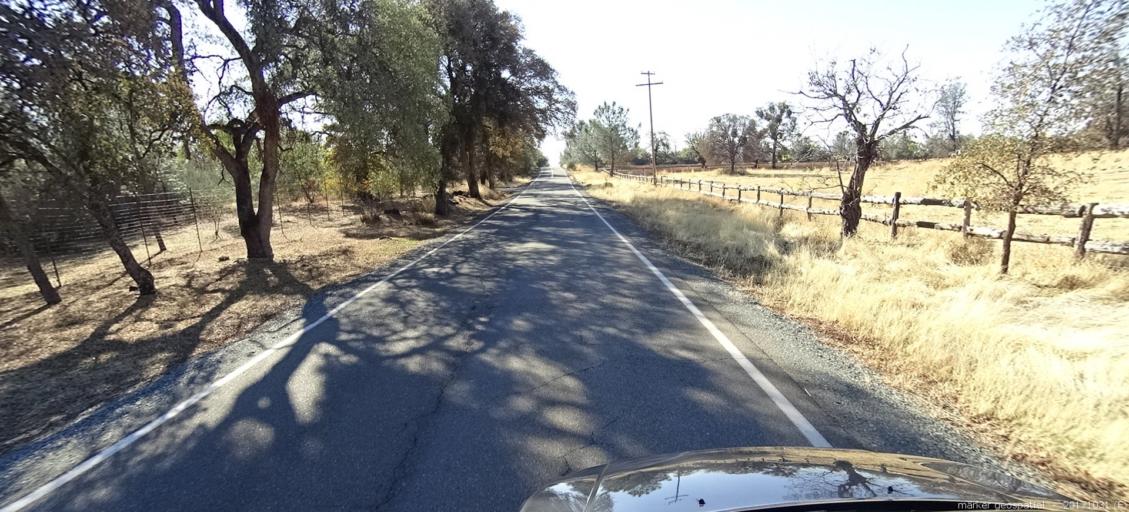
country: US
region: California
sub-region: Shasta County
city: Shingletown
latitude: 40.4532
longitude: -121.8994
